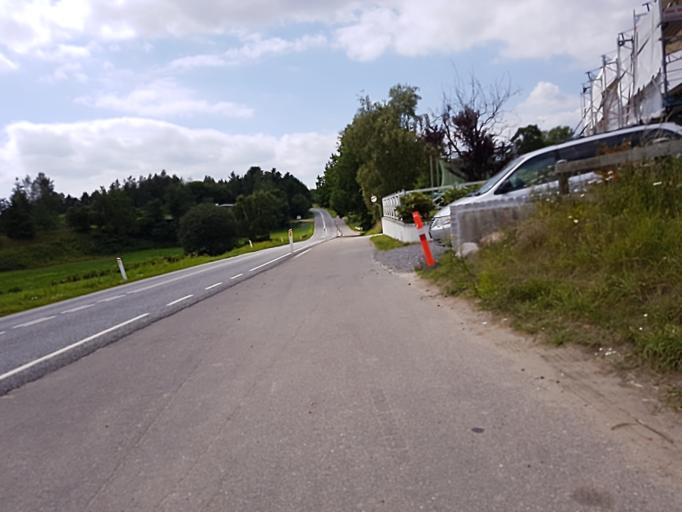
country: DK
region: Capital Region
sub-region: Ballerup Kommune
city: Malov
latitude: 55.7899
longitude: 12.3101
